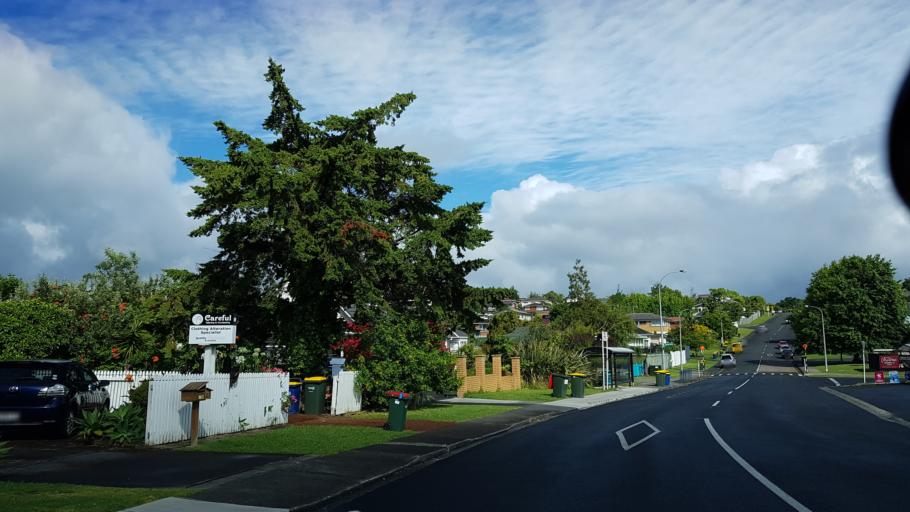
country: NZ
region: Auckland
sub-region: Auckland
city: North Shore
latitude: -36.7965
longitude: 174.7367
